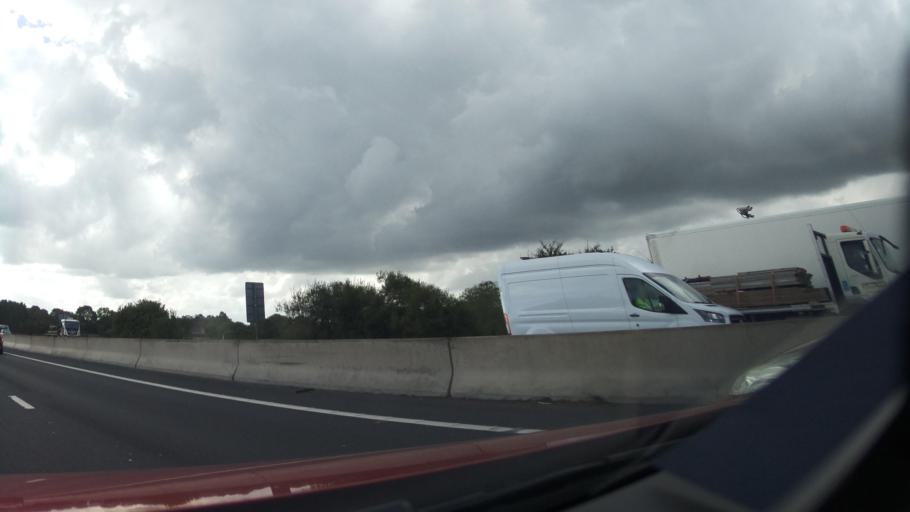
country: GB
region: England
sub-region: Cheshire East
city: Peover Superior
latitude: 53.2476
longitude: -2.4015
